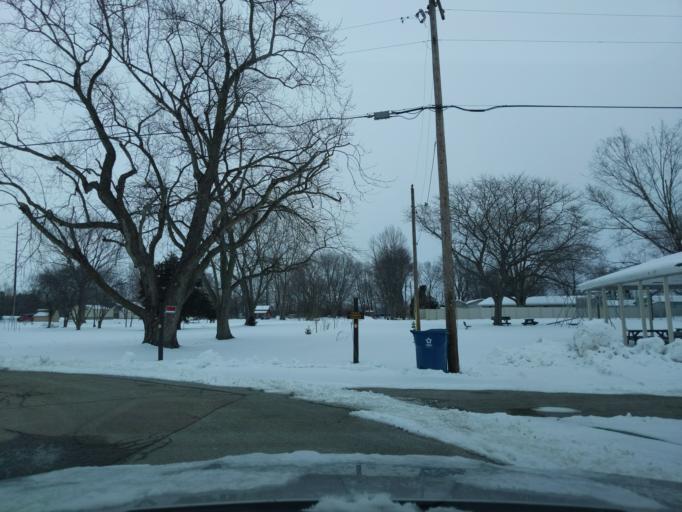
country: US
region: Indiana
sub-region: Benton County
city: Otterbein
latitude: 40.4859
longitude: -87.0939
